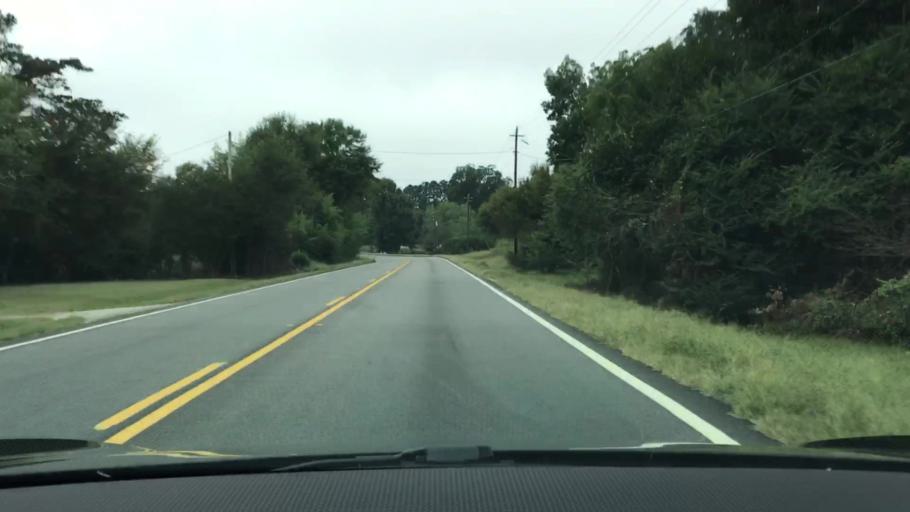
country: US
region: Georgia
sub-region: Greene County
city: Greensboro
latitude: 33.5646
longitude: -83.1460
